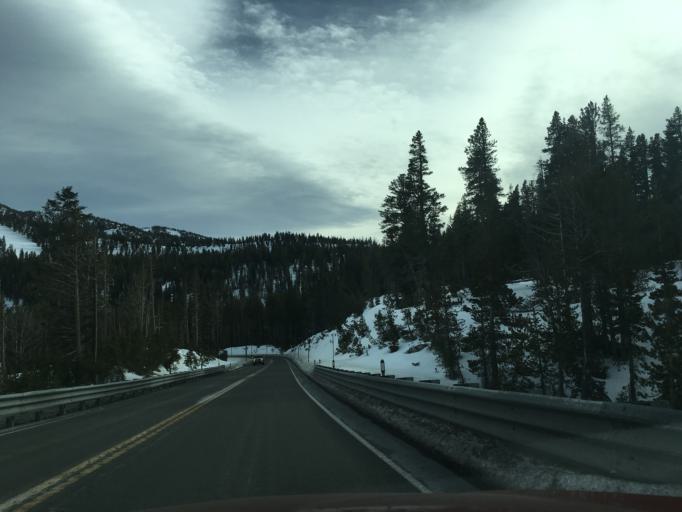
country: US
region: Nevada
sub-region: Washoe County
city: Incline Village
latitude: 39.3220
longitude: -119.9002
